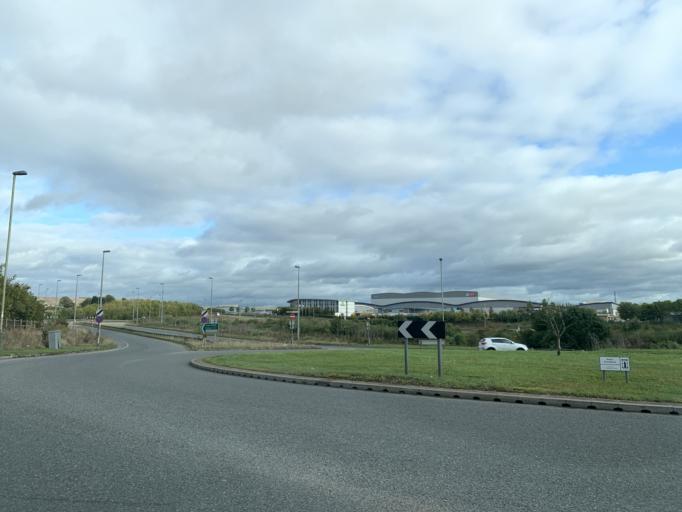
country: GB
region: England
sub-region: Wiltshire
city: Bulford
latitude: 51.1794
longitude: -1.7605
